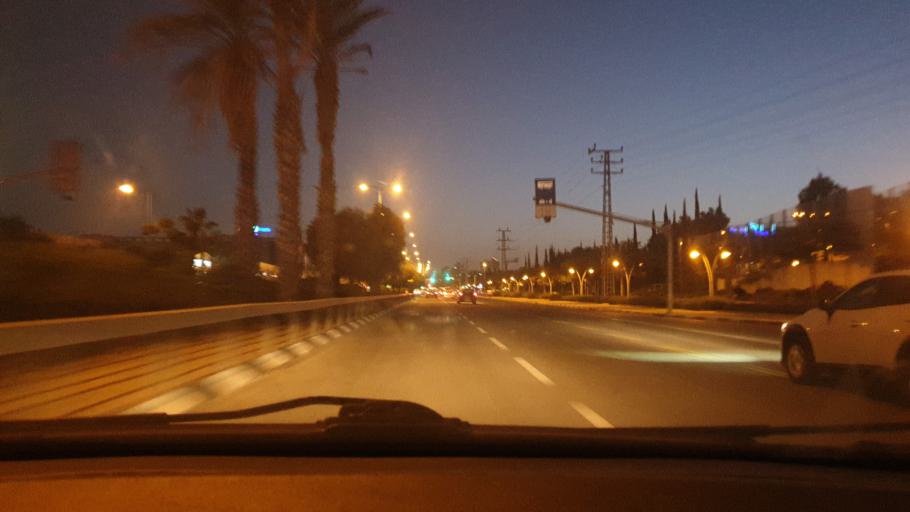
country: IL
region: Central District
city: Bet Dagan
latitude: 31.9829
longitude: 34.8100
